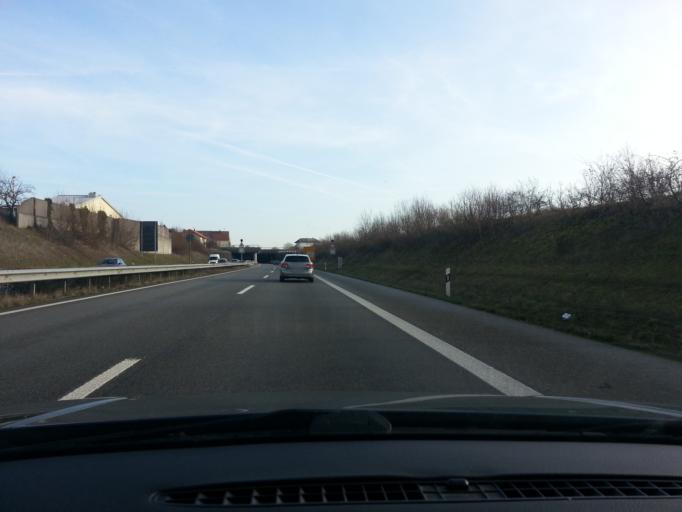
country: DE
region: Rheinland-Pfalz
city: Petersberg
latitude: 49.2321
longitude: 7.5753
